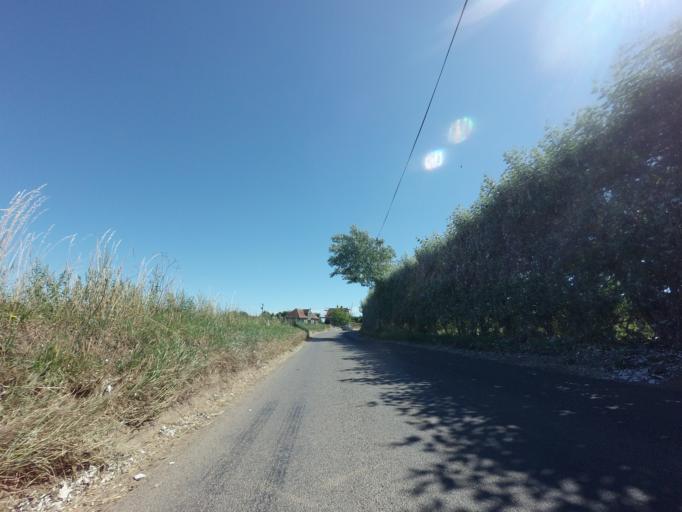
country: GB
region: England
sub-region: Kent
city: Ash
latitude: 51.2827
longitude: 1.2549
